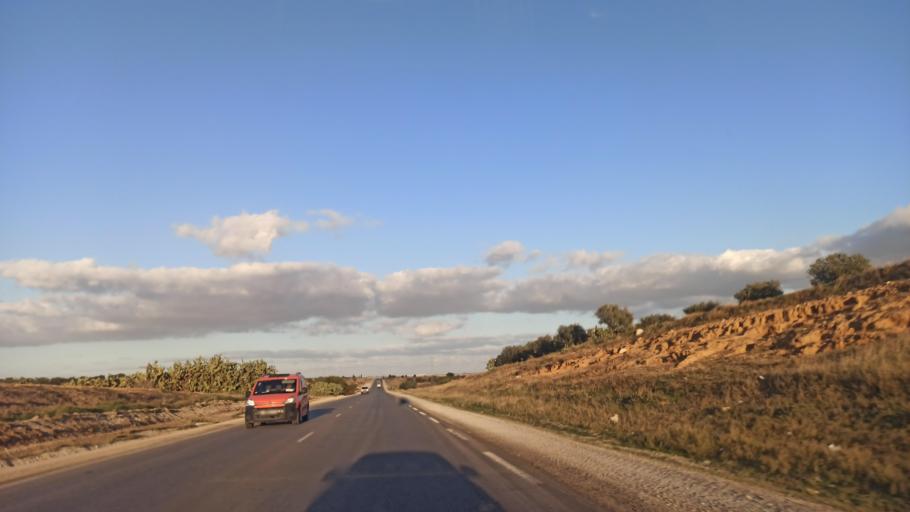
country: TN
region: Al Qayrawan
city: Sbikha
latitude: 35.8837
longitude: 10.2345
